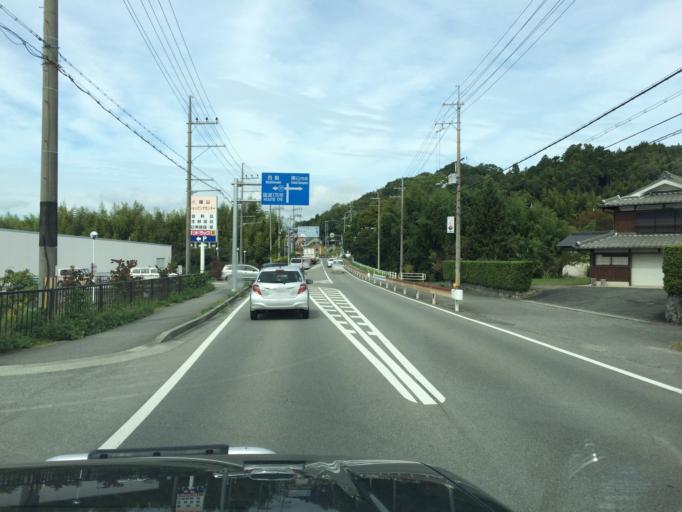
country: JP
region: Hyogo
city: Sasayama
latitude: 35.0737
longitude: 135.2071
